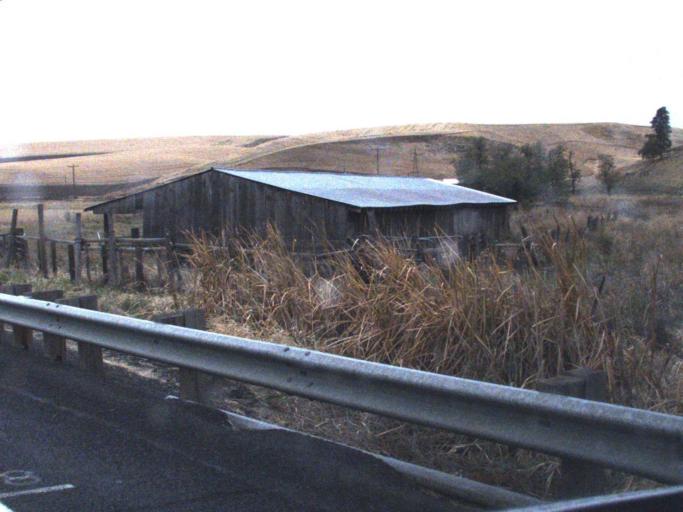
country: US
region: Washington
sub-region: Whitman County
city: Colfax
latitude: 46.8060
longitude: -117.5719
